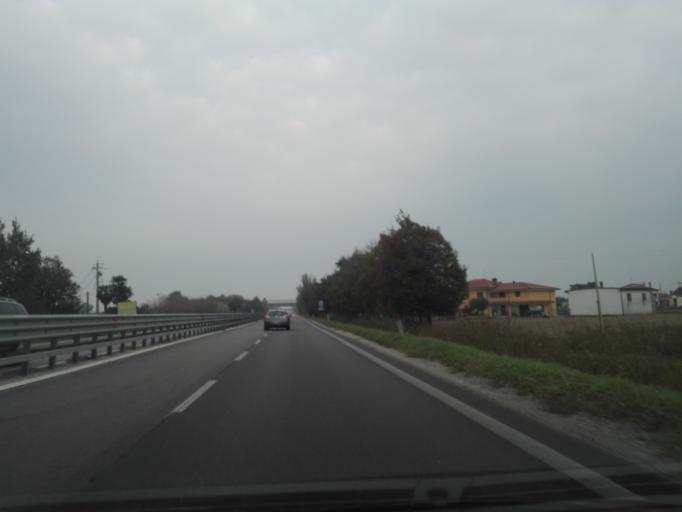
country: IT
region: Veneto
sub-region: Provincia di Verona
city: Spinimbecco
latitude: 45.1360
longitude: 11.3638
